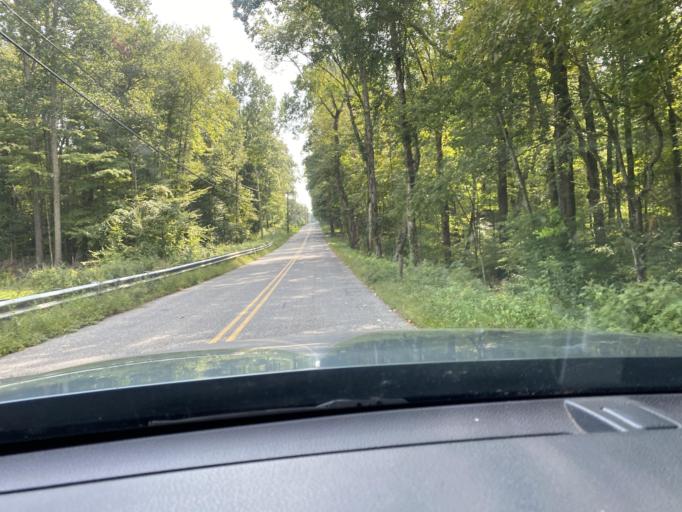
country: US
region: Connecticut
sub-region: Tolland County
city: Hebron
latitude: 41.6404
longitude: -72.2944
